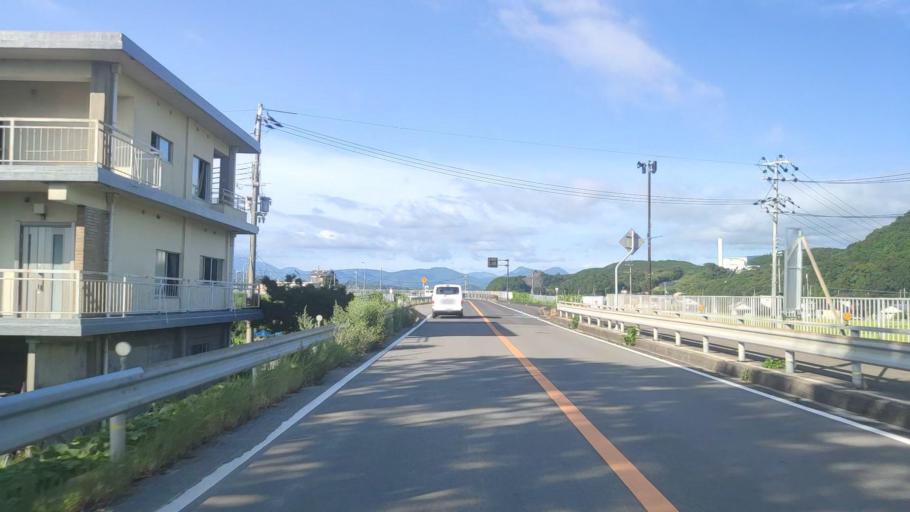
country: JP
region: Wakayama
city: Tanabe
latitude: 33.6781
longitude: 135.4090
